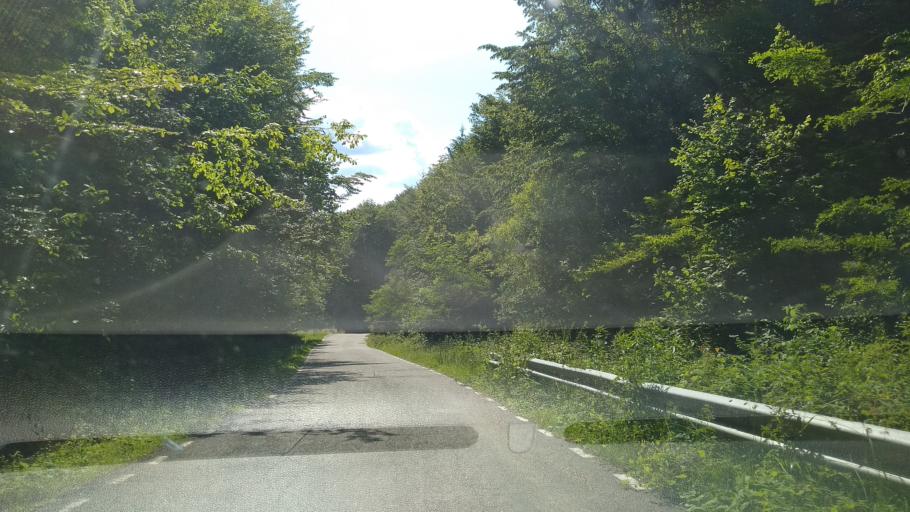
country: RO
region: Hunedoara
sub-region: Comuna Orastioara de Sus
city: Orastioara de Sus
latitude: 45.6220
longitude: 23.2957
